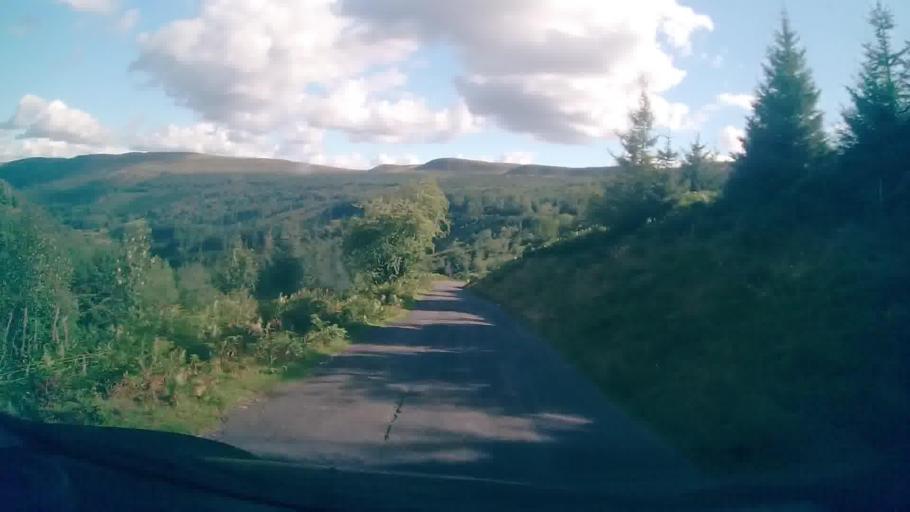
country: GB
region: Wales
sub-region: Merthyr Tydfil County Borough
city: Merthyr Tydfil
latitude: 51.8470
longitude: -3.3704
